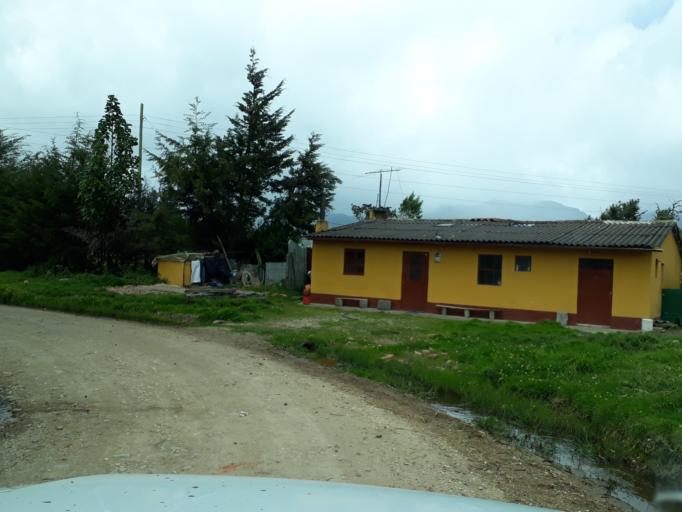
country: CO
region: Cundinamarca
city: Guasca
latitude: 4.8506
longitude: -73.9039
